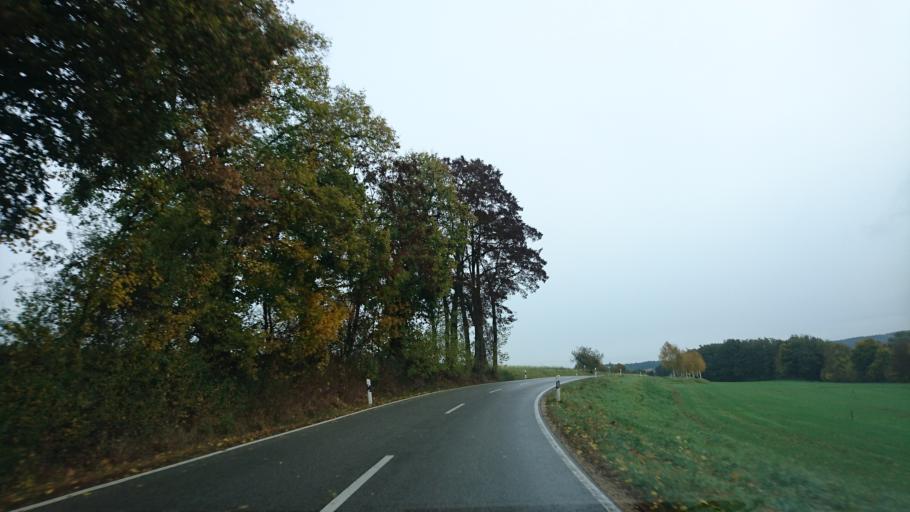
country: DE
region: Bavaria
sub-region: Regierungsbezirk Mittelfranken
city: Thalmassing
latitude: 49.1255
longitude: 11.1934
